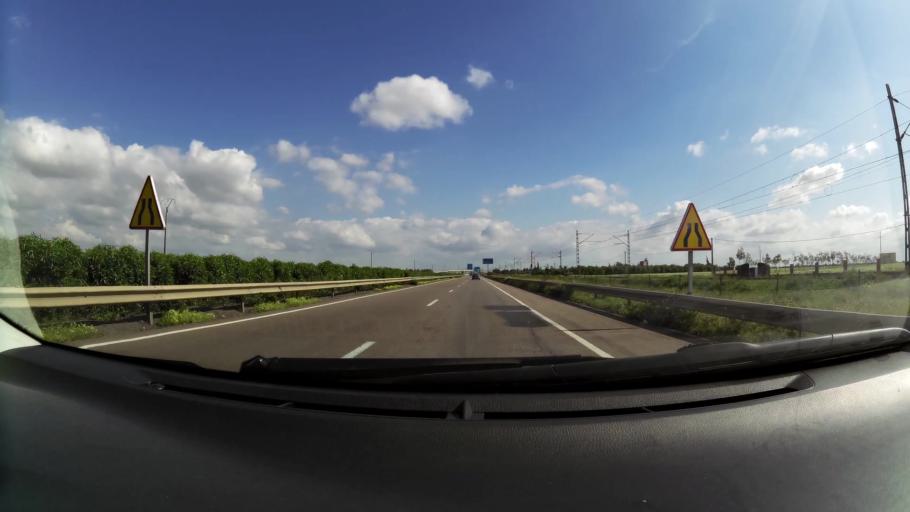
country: MA
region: Chaouia-Ouardigha
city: Nouaseur
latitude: 33.3313
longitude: -7.6088
